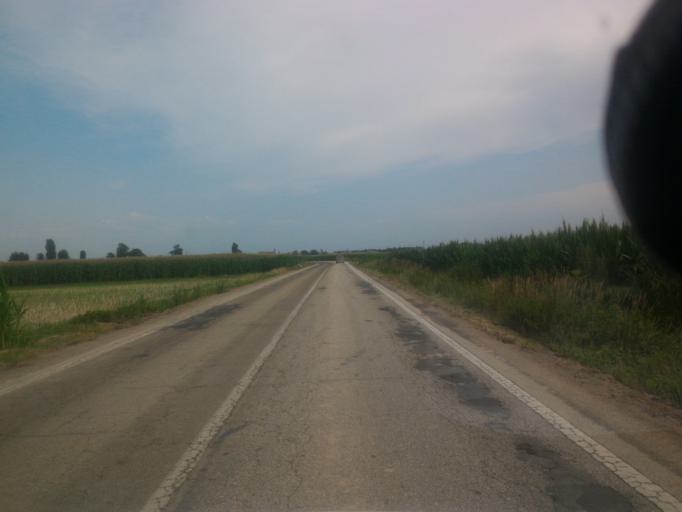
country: IT
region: Piedmont
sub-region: Provincia di Torino
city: Vigone
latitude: 44.8502
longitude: 7.4683
